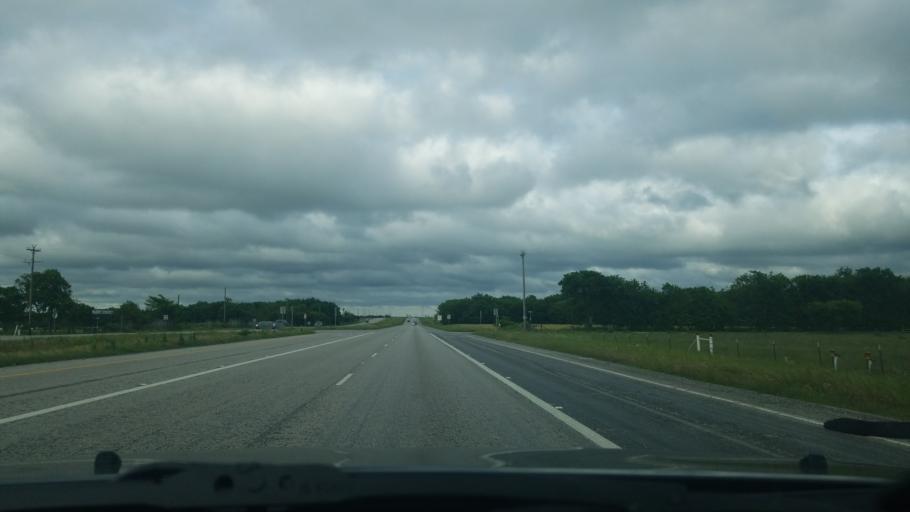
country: US
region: Texas
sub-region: Denton County
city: Ponder
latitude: 33.2384
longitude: -97.3223
